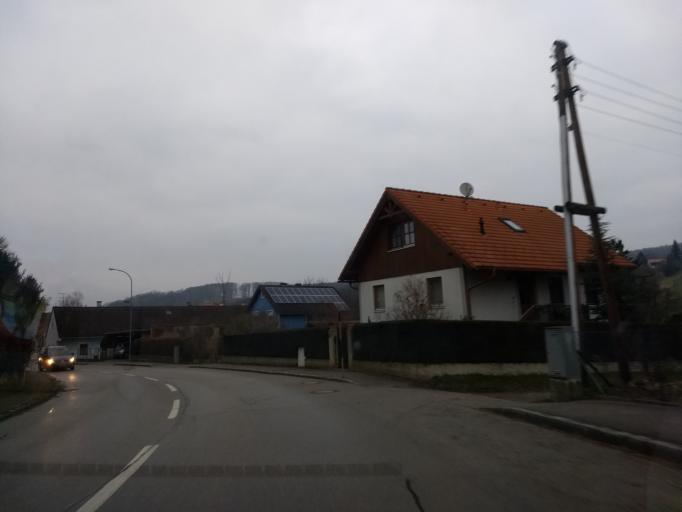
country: AT
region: Lower Austria
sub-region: Politischer Bezirk Tulln
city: Sieghartskirchen
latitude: 48.2296
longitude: 16.0229
